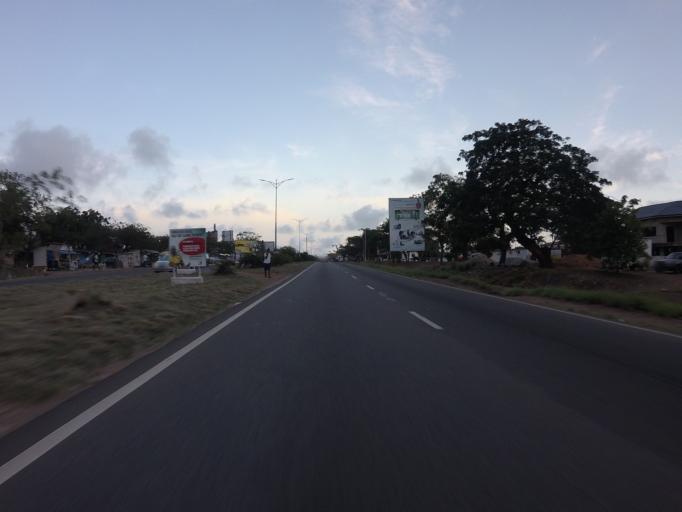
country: GH
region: Greater Accra
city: Accra
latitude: 5.5631
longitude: -0.1740
